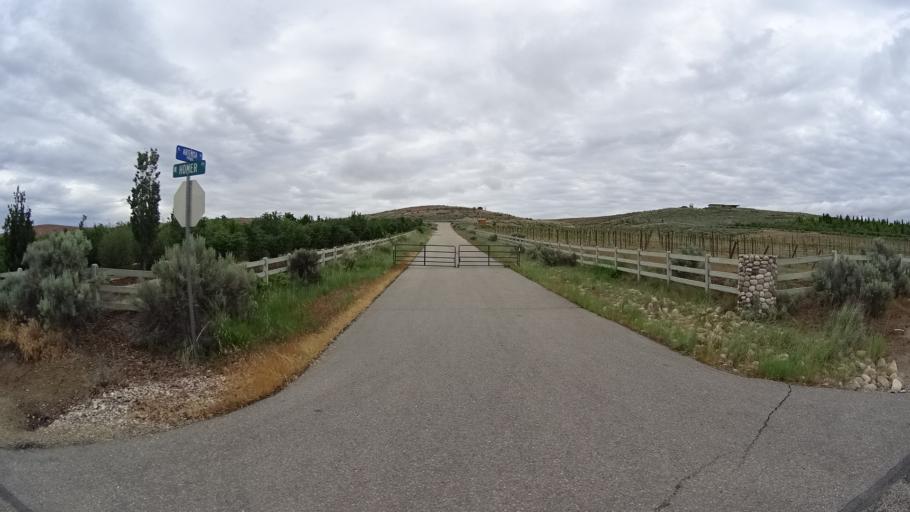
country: US
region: Idaho
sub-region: Ada County
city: Eagle
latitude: 43.7353
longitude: -116.4014
